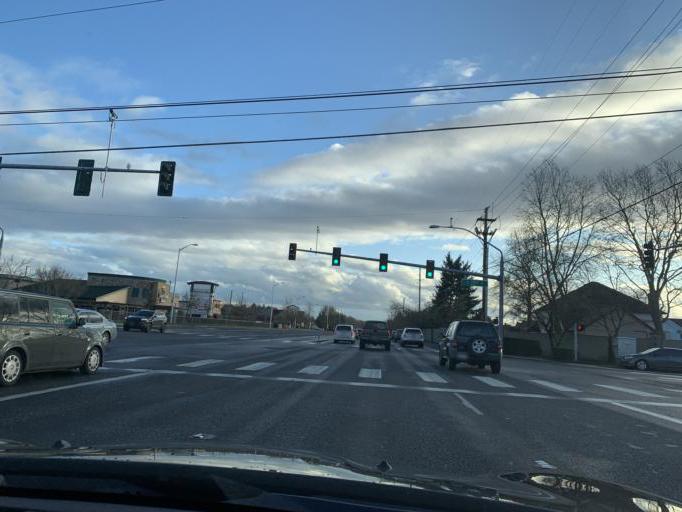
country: US
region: Washington
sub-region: Clark County
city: Mill Plain
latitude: 45.6105
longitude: -122.5042
